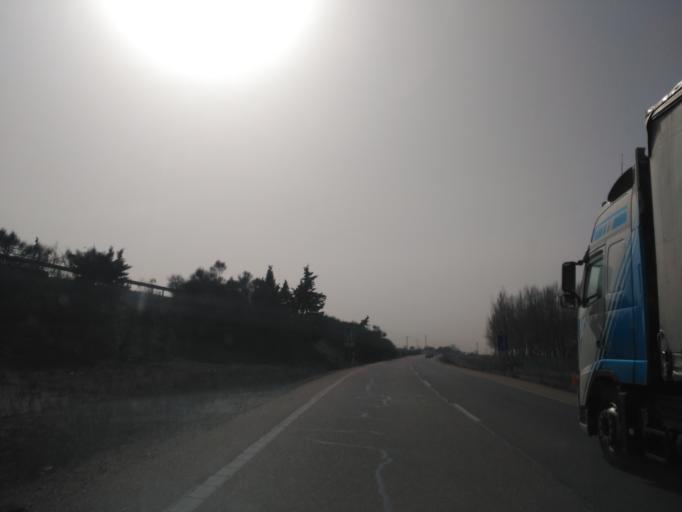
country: ES
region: Castille and Leon
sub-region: Provincia de Palencia
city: Venta de Banos
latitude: 41.9299
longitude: -4.5033
